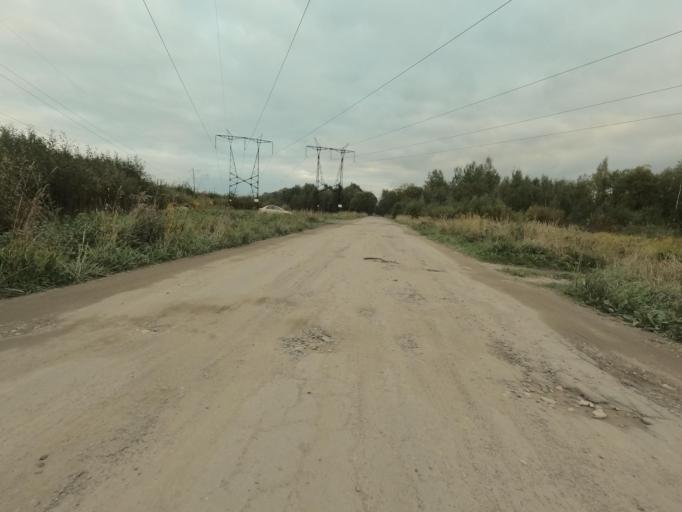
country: RU
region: St.-Petersburg
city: Sapernyy
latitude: 59.7593
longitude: 30.6572
